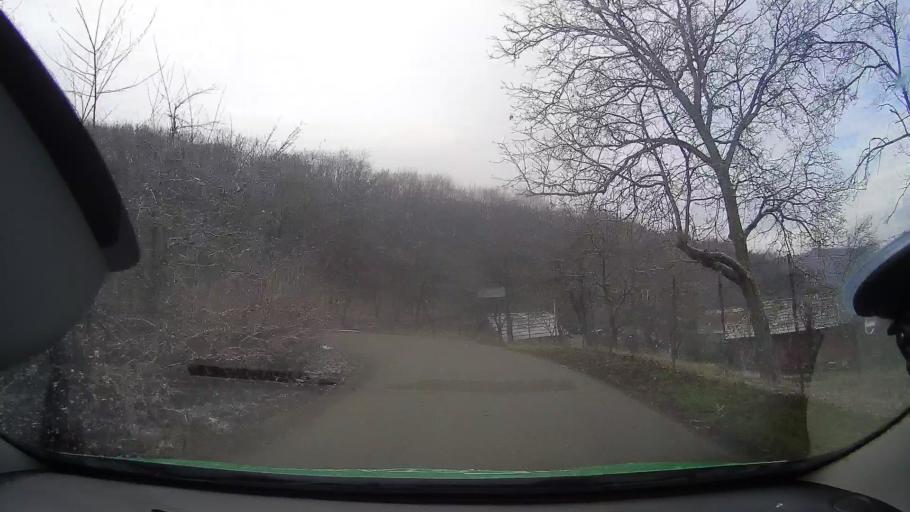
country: RO
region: Mures
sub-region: Comuna Chetani
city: Chetani
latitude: 46.4036
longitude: 24.0133
